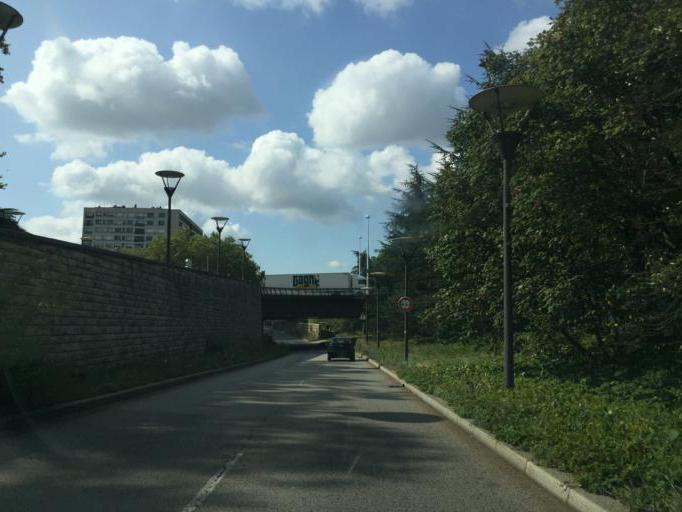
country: FR
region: Rhone-Alpes
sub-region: Departement du Rhone
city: Caluire-et-Cuire
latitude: 45.7789
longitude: 4.8450
